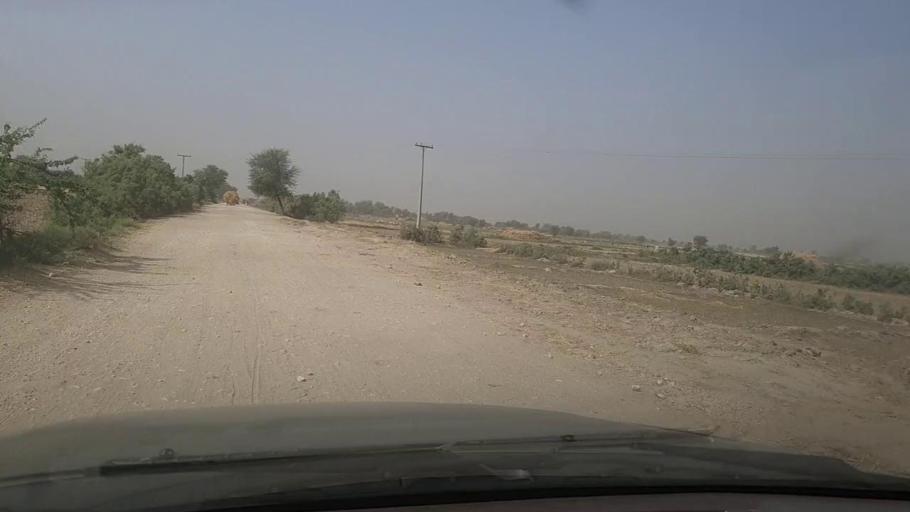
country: PK
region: Sindh
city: Shikarpur
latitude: 27.8993
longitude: 68.5898
